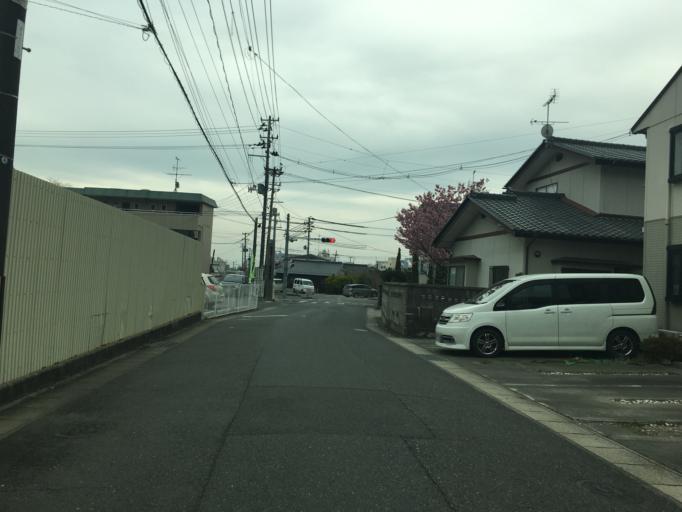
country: JP
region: Fukushima
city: Iwaki
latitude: 36.9514
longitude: 140.9109
